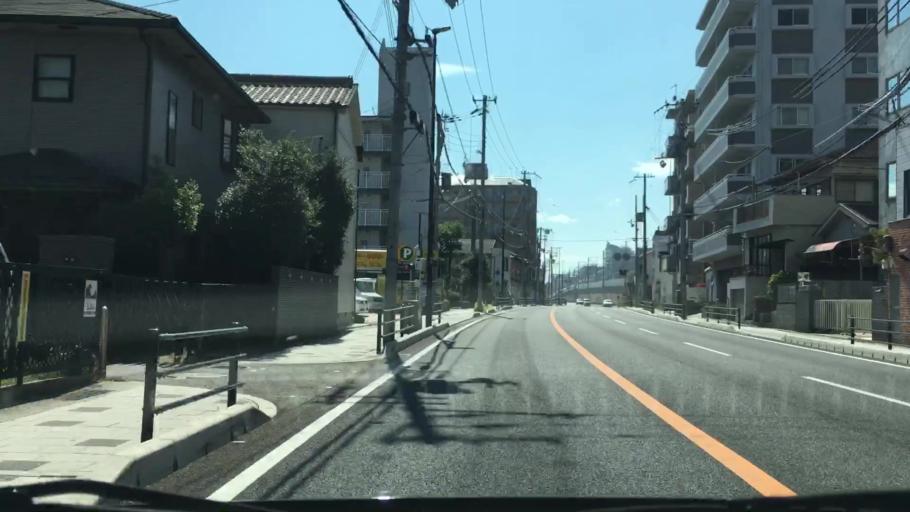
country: JP
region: Hyogo
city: Akashi
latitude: 34.6328
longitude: 135.0811
